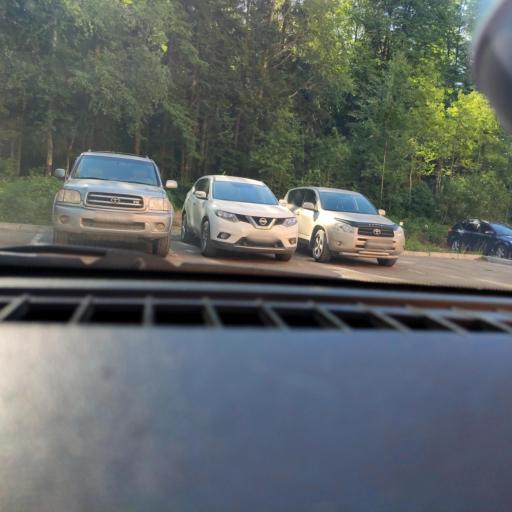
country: RU
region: Perm
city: Perm
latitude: 58.0826
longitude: 56.4071
